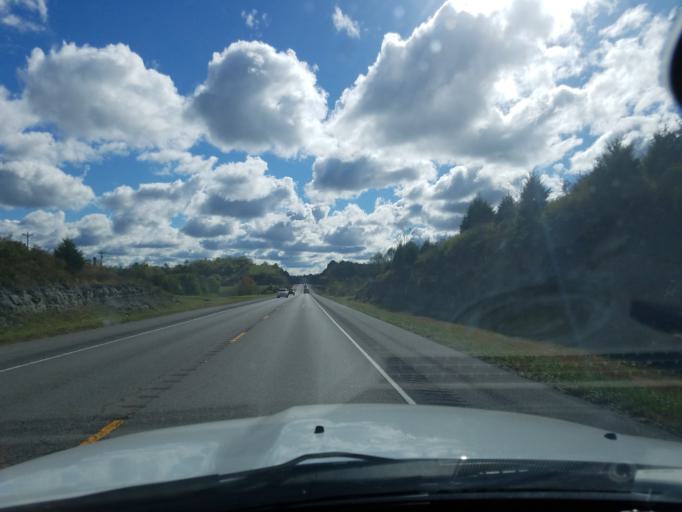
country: US
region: Kentucky
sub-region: Lincoln County
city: Stanford
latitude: 37.5076
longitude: -84.5860
